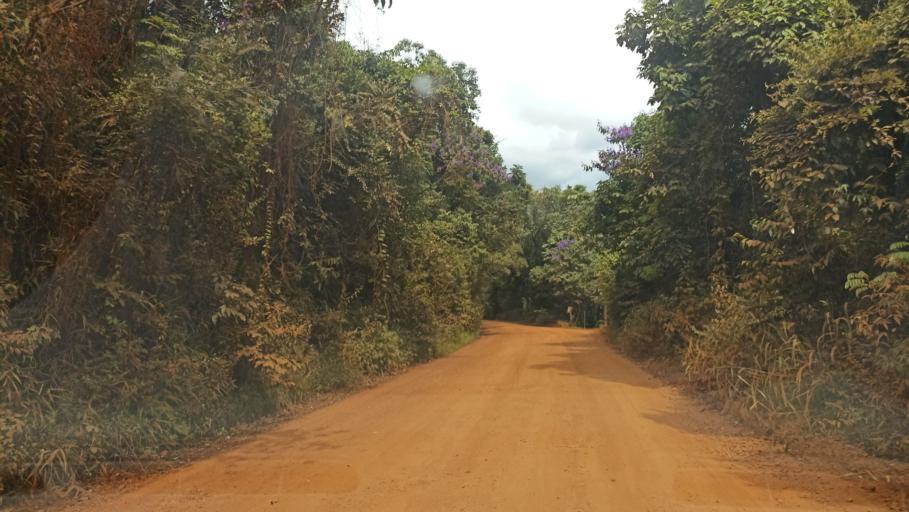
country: BR
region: Minas Gerais
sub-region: Itabirito
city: Itabirito
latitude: -20.3785
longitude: -43.7628
